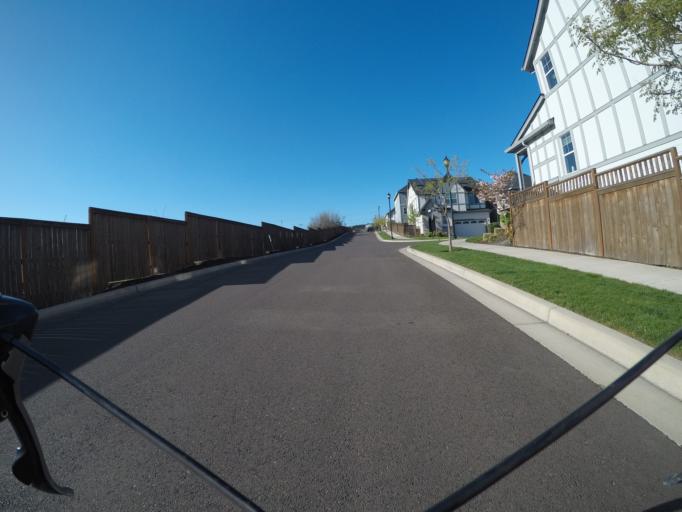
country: US
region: Oregon
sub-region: Washington County
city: King City
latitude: 45.4246
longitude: -122.8568
